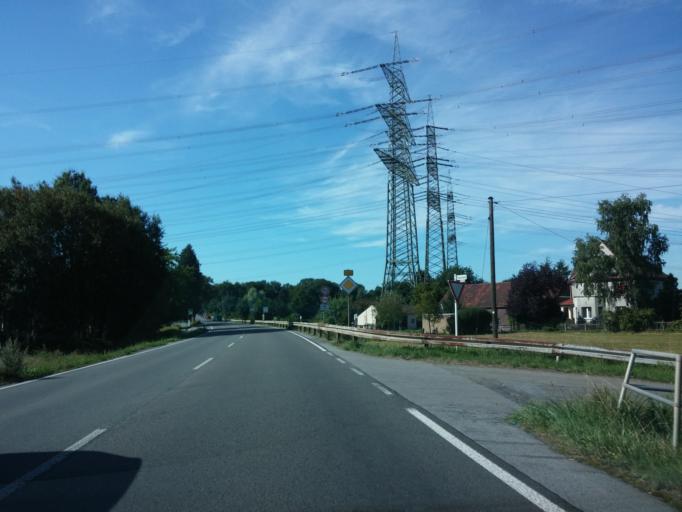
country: DE
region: North Rhine-Westphalia
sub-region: Regierungsbezirk Munster
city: Gladbeck
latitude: 51.6244
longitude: 7.0120
